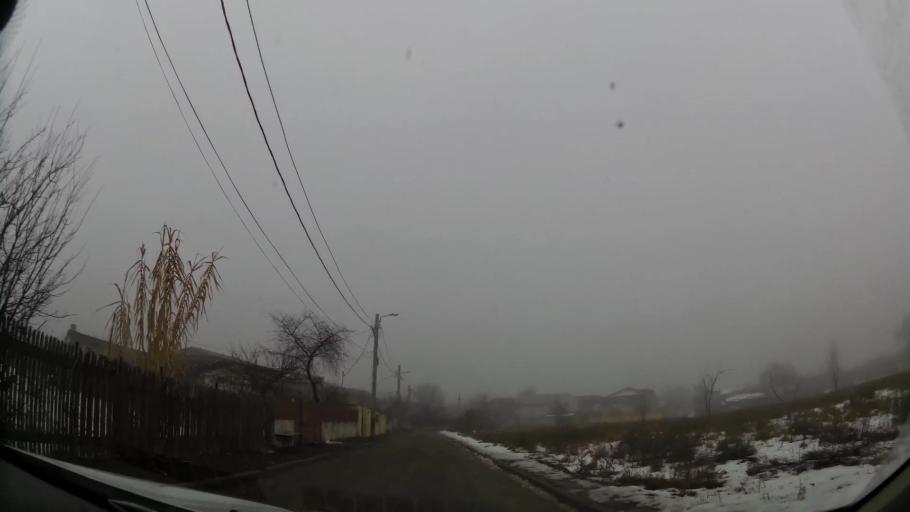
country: RO
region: Ilfov
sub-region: Comuna Chiajna
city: Rosu
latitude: 44.4706
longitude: 26.0131
